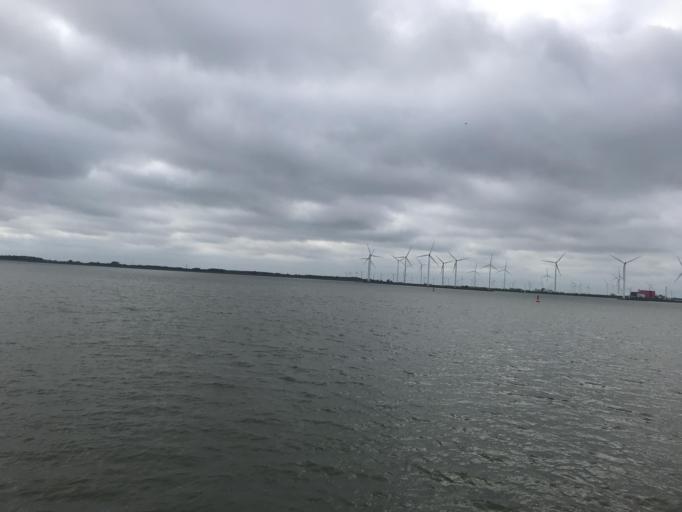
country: NL
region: Groningen
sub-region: Gemeente Delfzijl
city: Delfzijl
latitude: 53.3276
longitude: 7.0245
